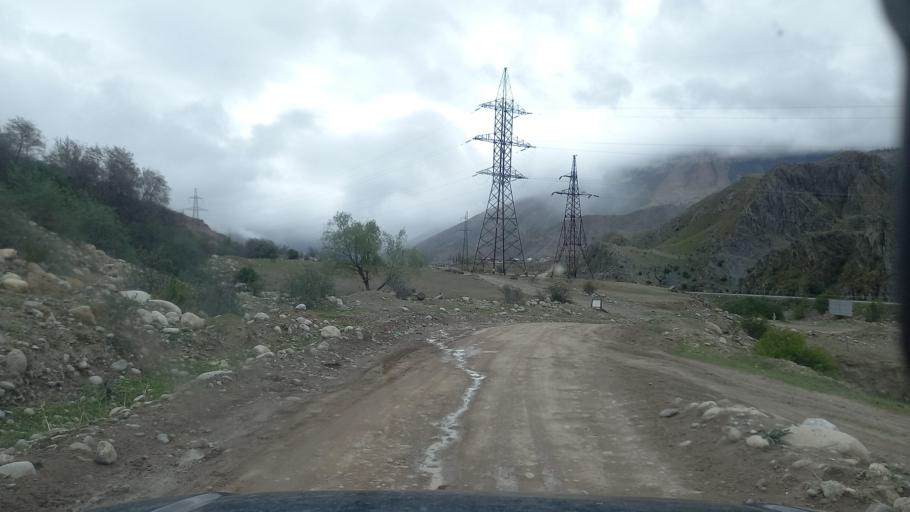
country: RU
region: Kabardino-Balkariya
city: Bylym
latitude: 43.4585
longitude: 43.0114
